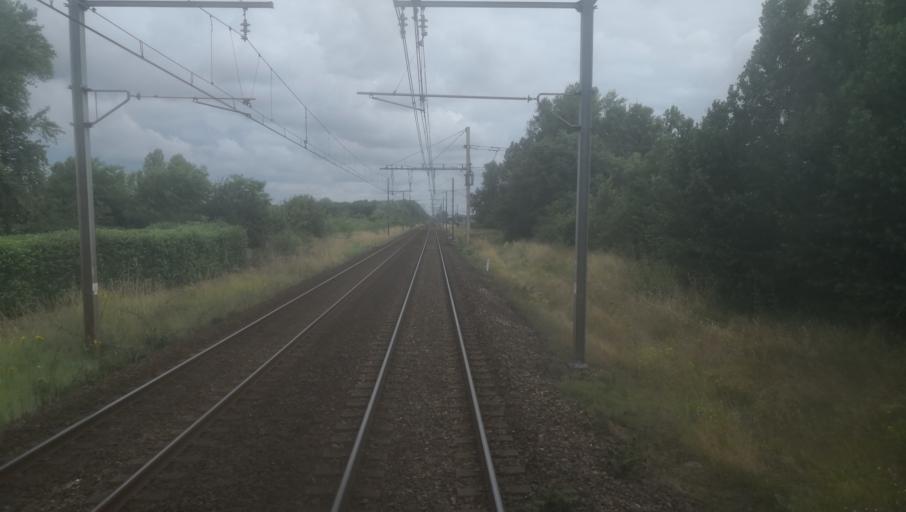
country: FR
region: Aquitaine
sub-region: Departement de la Gironde
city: Villenave-d'Ornon
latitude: 44.7804
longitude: -0.5511
